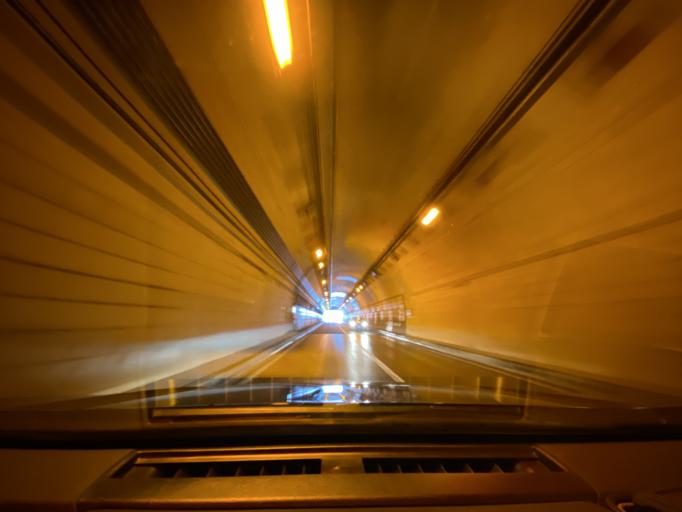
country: JP
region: Hokkaido
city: Rumoi
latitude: 43.7914
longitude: 141.3732
